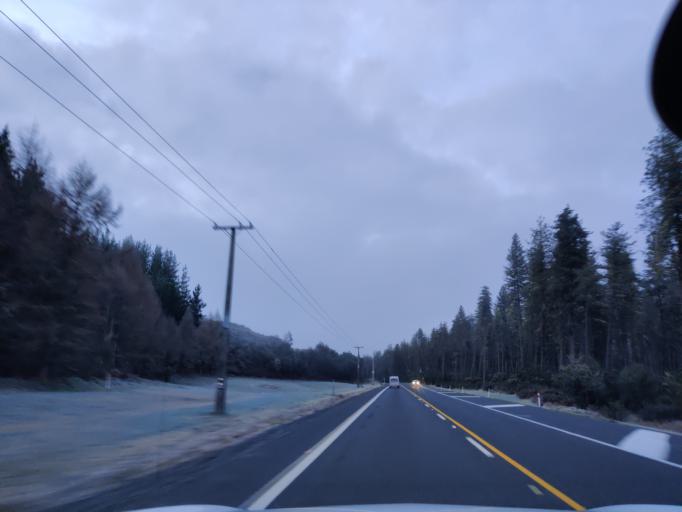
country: NZ
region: Waikato
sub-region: South Waikato District
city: Tokoroa
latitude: -38.3802
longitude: 176.0029
